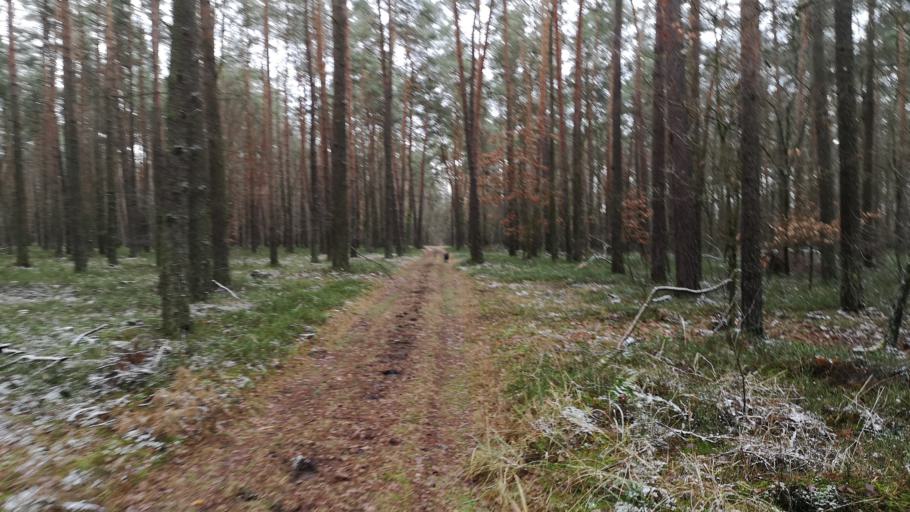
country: PL
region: Kujawsko-Pomorskie
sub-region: Powiat golubsko-dobrzynski
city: Ciechocin
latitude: 53.0795
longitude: 18.9613
